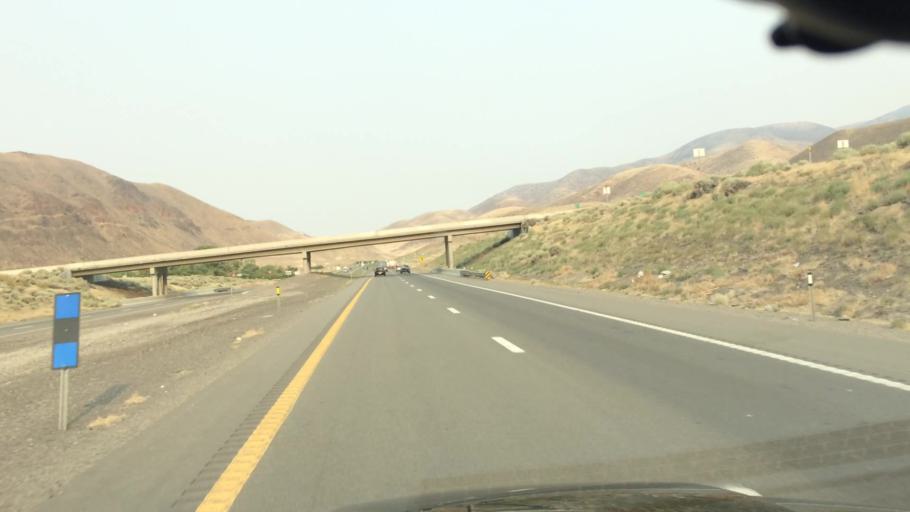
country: US
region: Nevada
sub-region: Lyon County
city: Fernley
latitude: 39.5895
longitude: -119.4271
